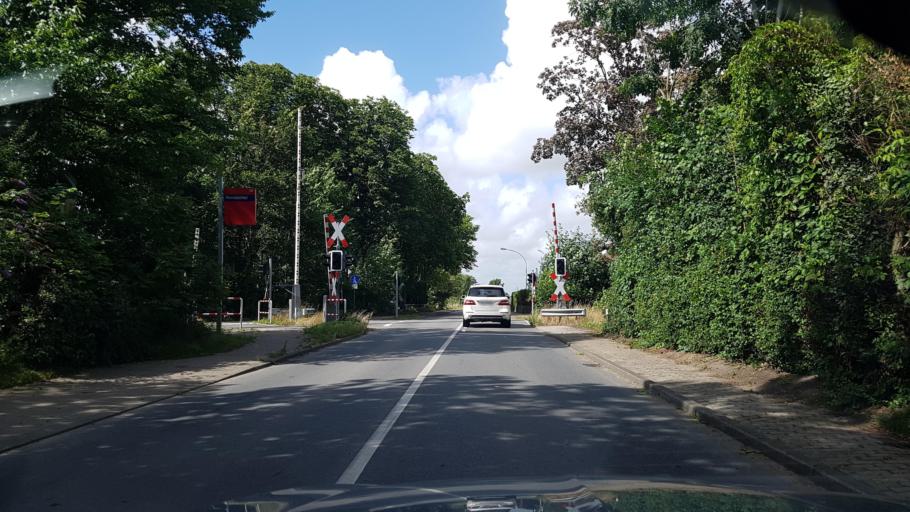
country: DE
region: Schleswig-Holstein
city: Reinsbuttel
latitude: 54.1809
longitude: 8.9074
